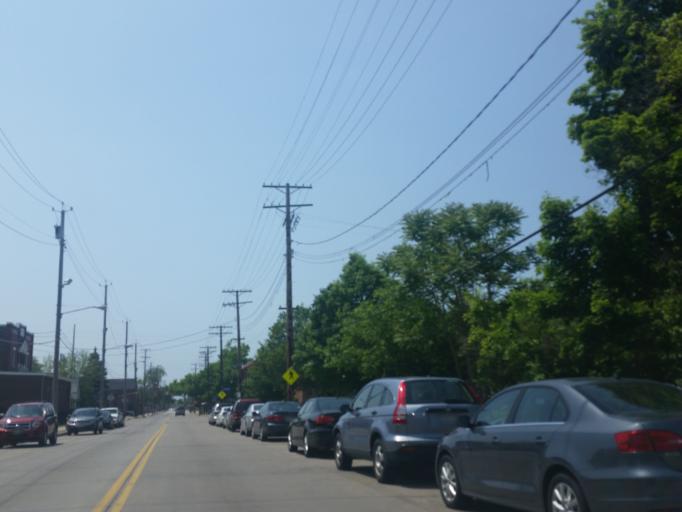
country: US
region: Ohio
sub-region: Cuyahoga County
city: Bratenahl
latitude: 41.4934
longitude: -81.6220
